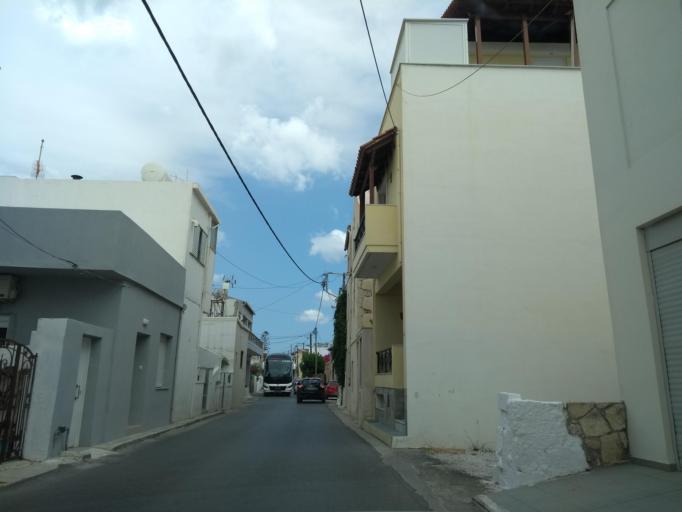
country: GR
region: Crete
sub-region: Nomos Chanias
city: Kalivai
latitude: 35.4558
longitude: 24.1694
